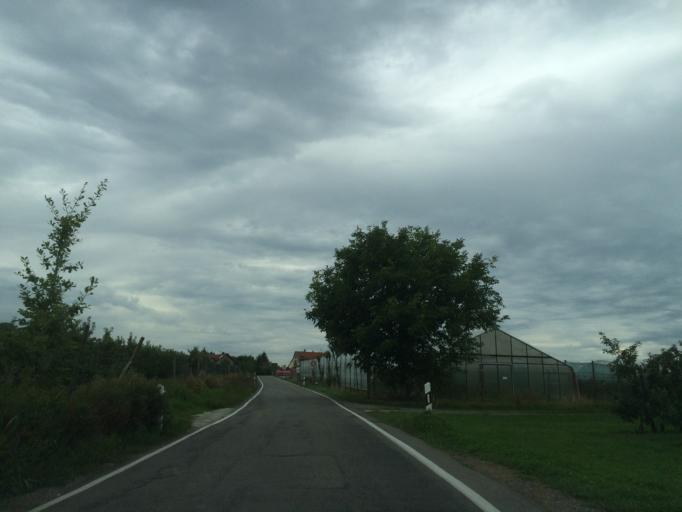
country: DE
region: Baden-Wuerttemberg
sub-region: Tuebingen Region
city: Immenstaad am Bodensee
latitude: 47.6829
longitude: 9.3494
